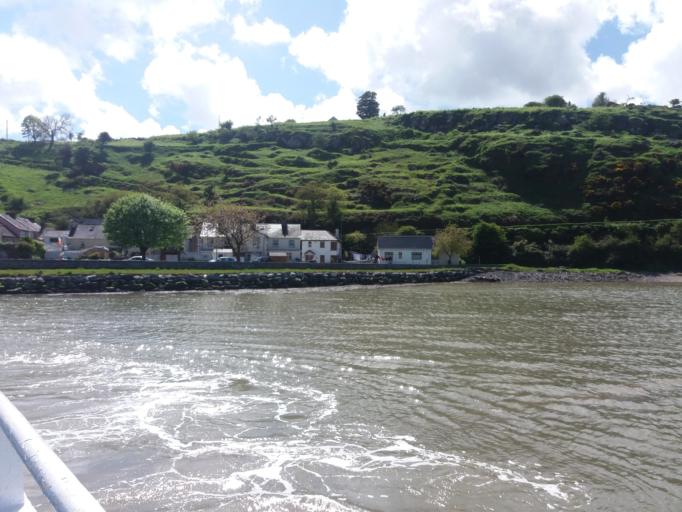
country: IE
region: Munster
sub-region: Waterford
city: Dunmore East
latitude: 52.2406
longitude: -6.9730
